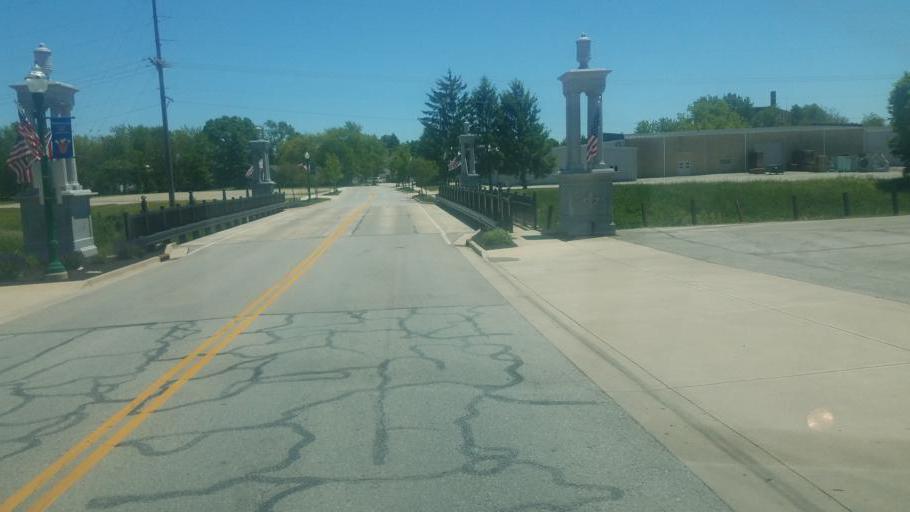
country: US
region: Ohio
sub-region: Darke County
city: Versailles
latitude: 40.2254
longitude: -84.4872
